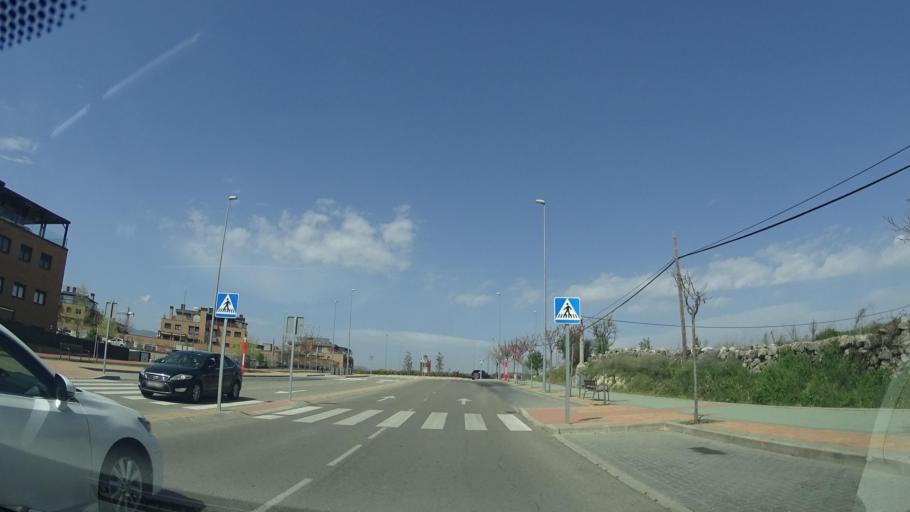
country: ES
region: Madrid
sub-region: Provincia de Madrid
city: Colmenar Viejo
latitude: 40.6762
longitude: -3.7697
